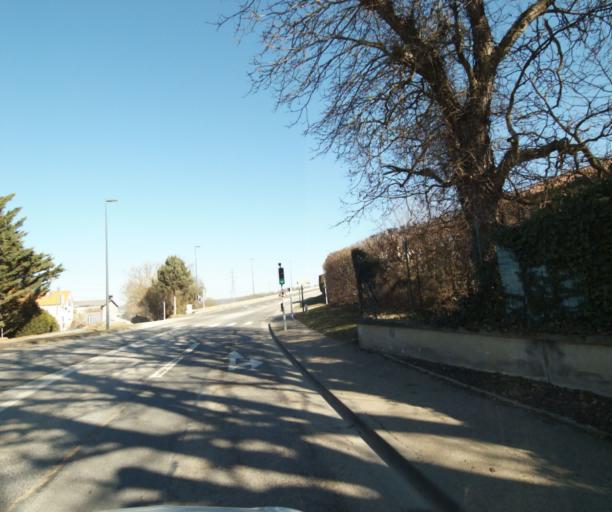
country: FR
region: Lorraine
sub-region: Departement de Meurthe-et-Moselle
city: Malzeville
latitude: 48.7235
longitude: 6.1766
